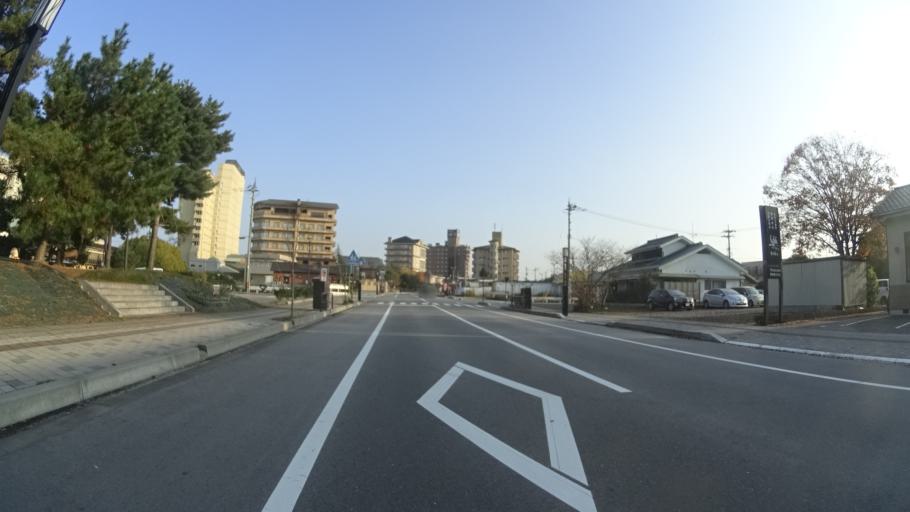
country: JP
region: Ishikawa
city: Nanao
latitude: 37.0865
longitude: 136.9241
